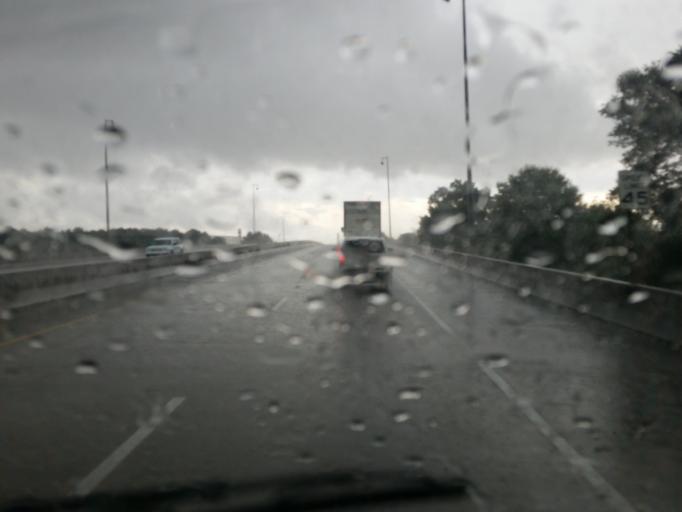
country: US
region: Alabama
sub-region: Mobile County
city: Prichard
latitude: 30.7306
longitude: -88.0652
